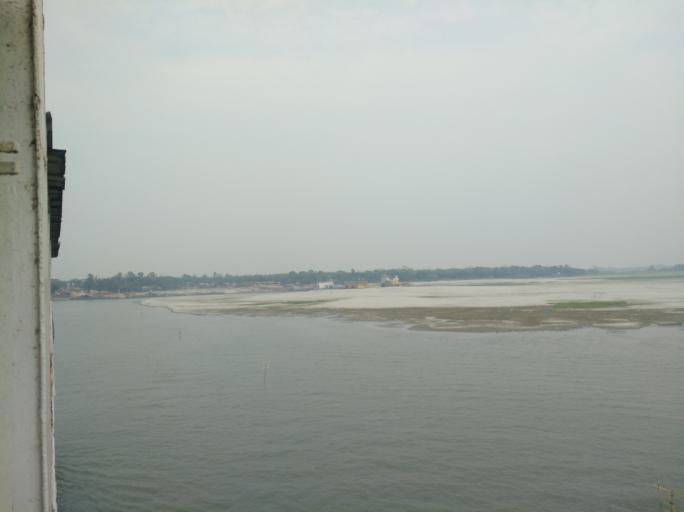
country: BD
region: Dhaka
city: Faridpur
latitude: 23.7819
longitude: 89.8085
